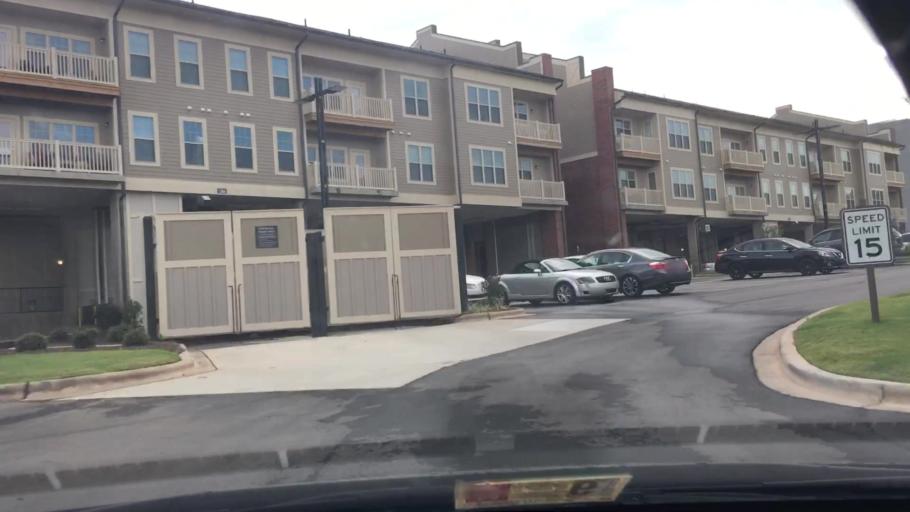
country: US
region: South Carolina
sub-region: York County
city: Fort Mill
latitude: 35.0273
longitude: -80.9620
